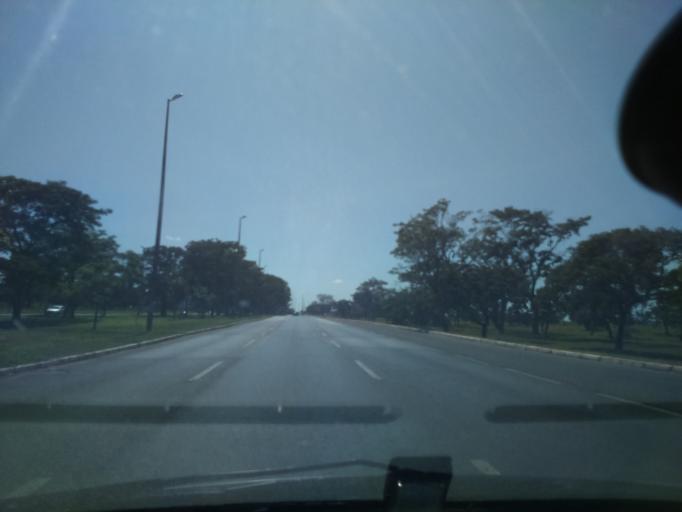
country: BR
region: Federal District
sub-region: Brasilia
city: Brasilia
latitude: -15.8114
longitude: -47.8640
